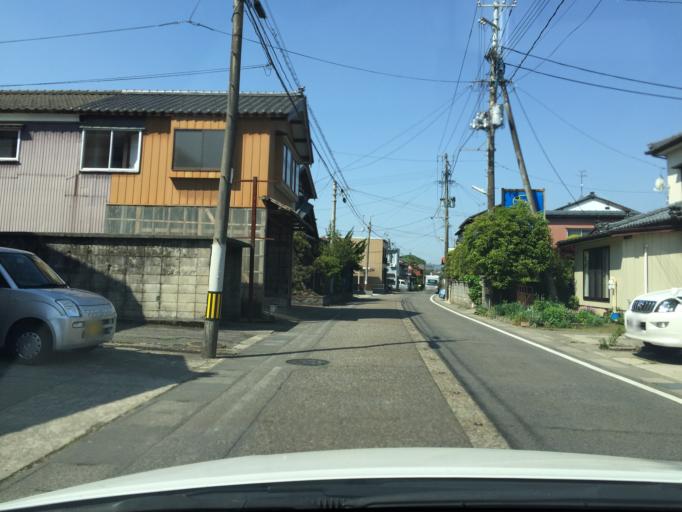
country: JP
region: Niigata
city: Muramatsu
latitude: 37.6961
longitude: 139.1818
